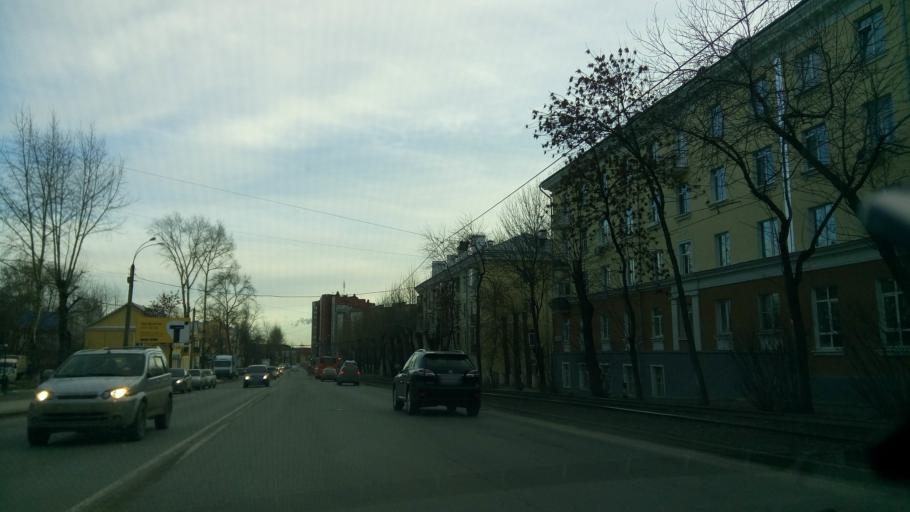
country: RU
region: Sverdlovsk
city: Shuvakish
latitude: 56.8735
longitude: 60.5187
